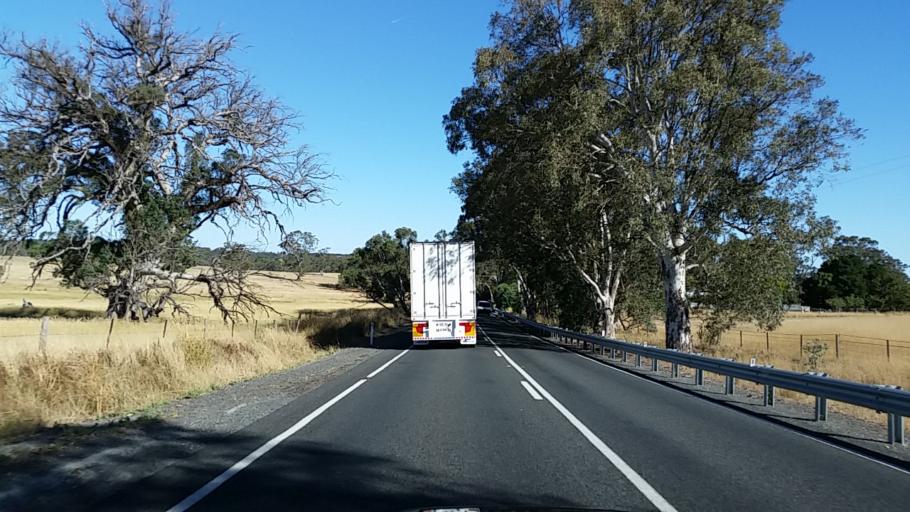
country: AU
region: South Australia
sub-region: Adelaide Hills
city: Birdwood
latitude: -34.7727
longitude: 139.0274
